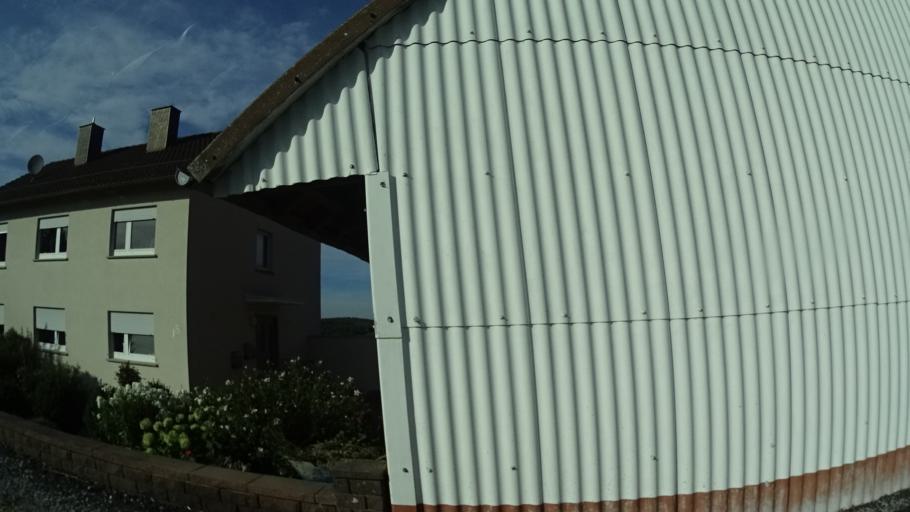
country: DE
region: Hesse
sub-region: Regierungsbezirk Kassel
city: Dipperz
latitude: 50.5330
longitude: 9.8378
